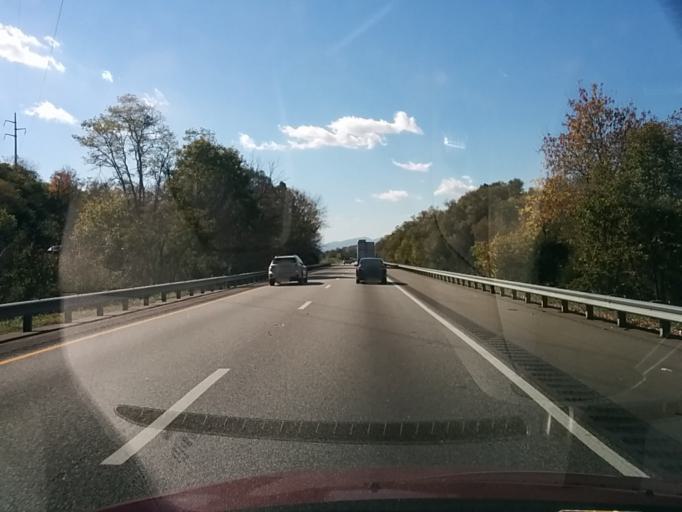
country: US
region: Virginia
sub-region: Botetourt County
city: Daleville
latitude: 37.4025
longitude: -79.8970
